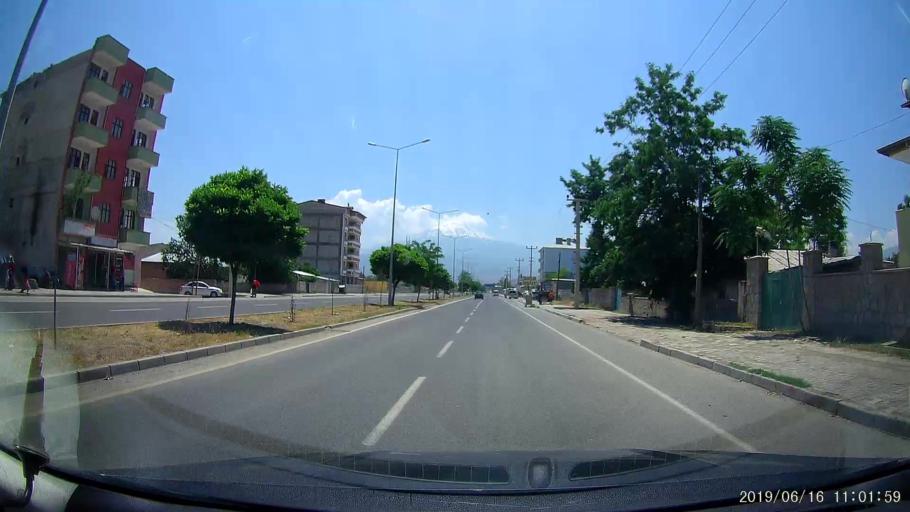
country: TR
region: Igdir
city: Igdir
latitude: 39.9107
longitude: 44.0554
